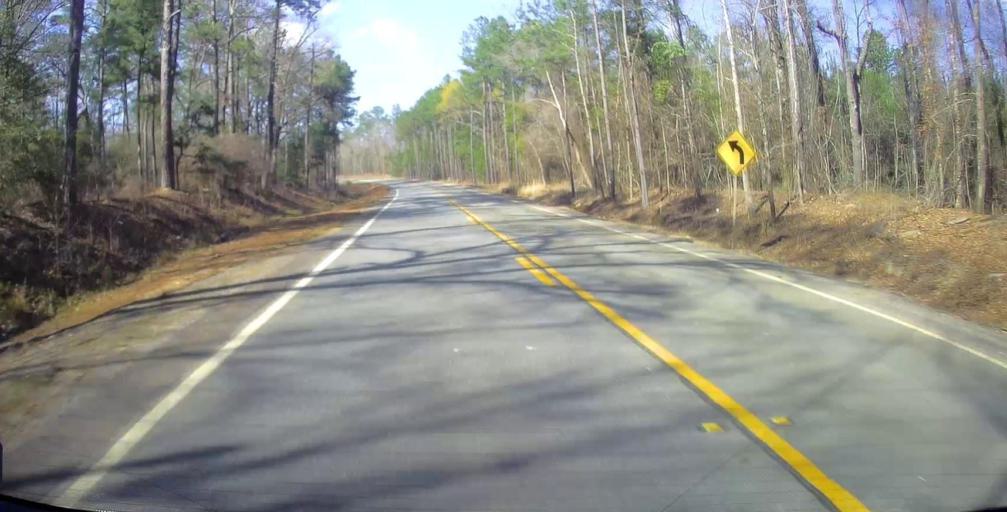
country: US
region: Georgia
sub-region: Wilkinson County
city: Gordon
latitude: 32.8204
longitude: -83.3250
